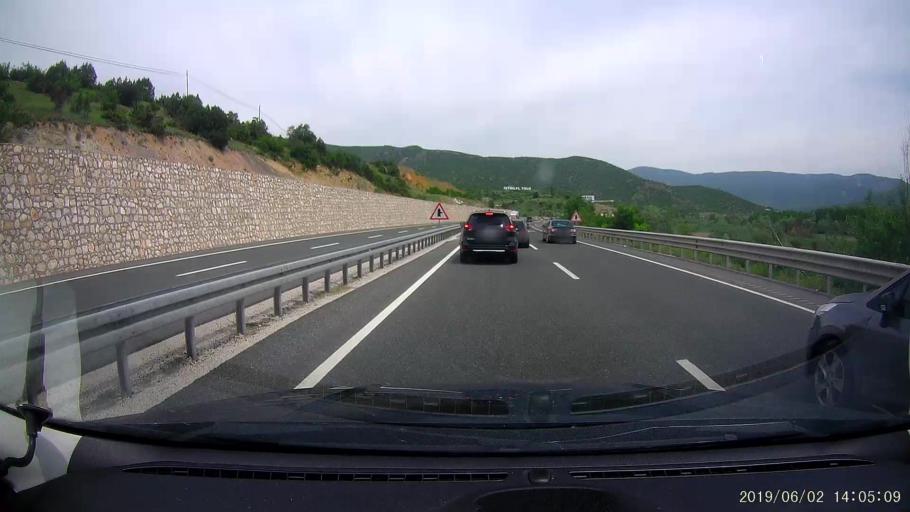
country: TR
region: Cankiri
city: Ilgaz
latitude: 40.9024
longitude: 33.6648
